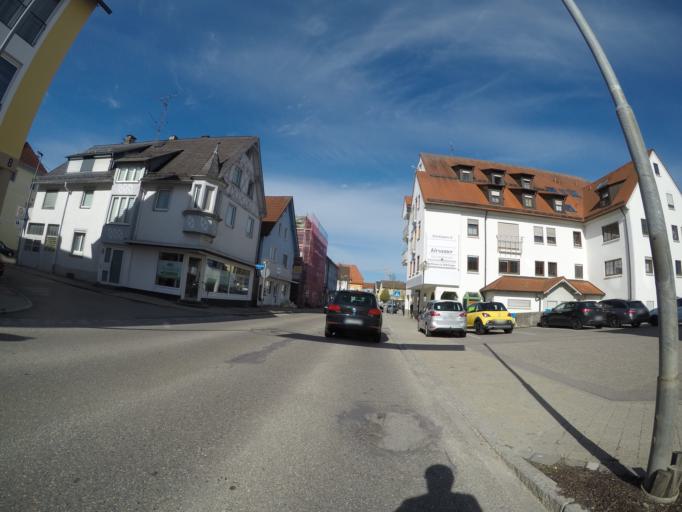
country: DE
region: Baden-Wuerttemberg
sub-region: Tuebingen Region
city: Laichingen
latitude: 48.4894
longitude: 9.6876
